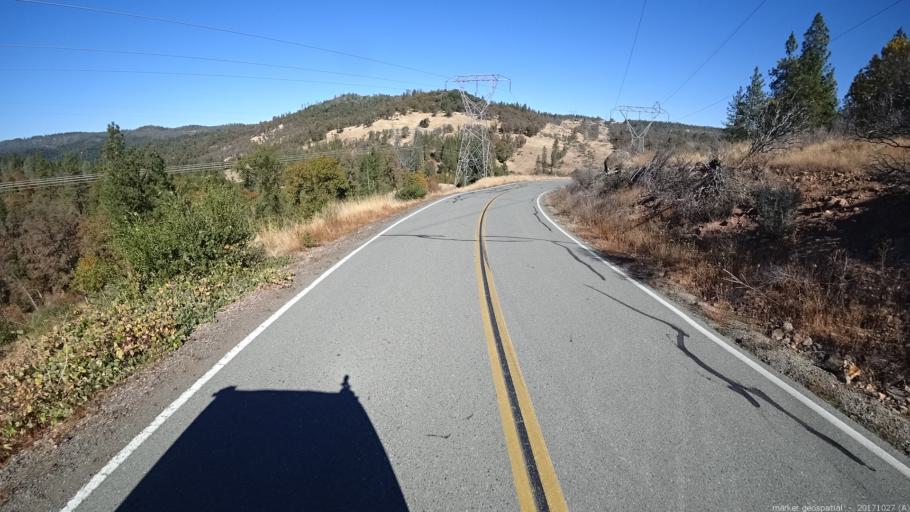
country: US
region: California
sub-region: Shasta County
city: Bella Vista
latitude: 40.7366
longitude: -122.0108
